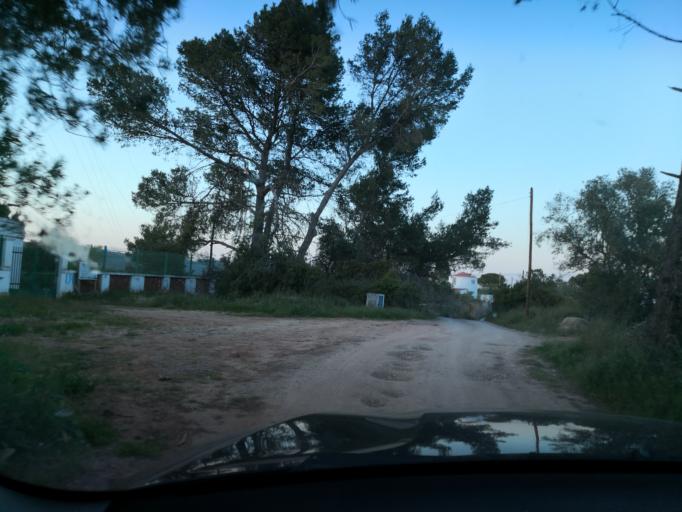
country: PT
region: Setubal
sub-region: Setubal
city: Setubal
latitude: 38.5235
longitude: -8.9184
